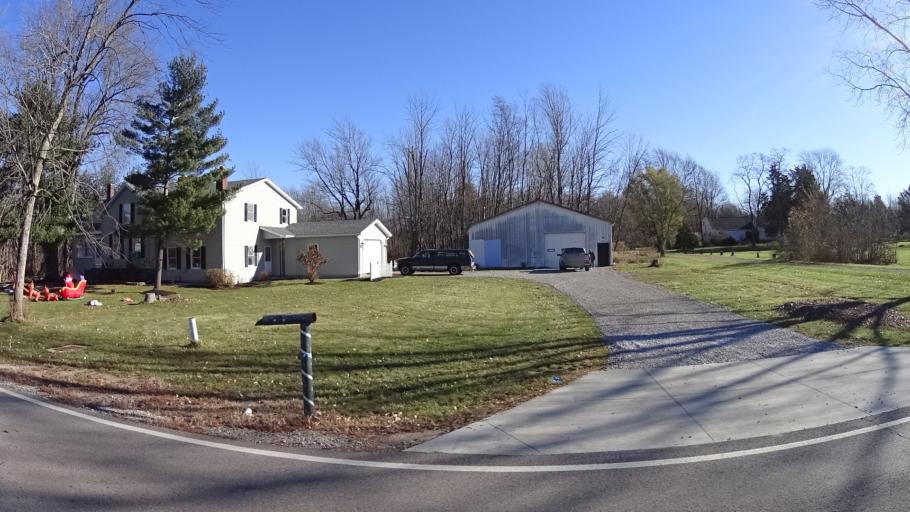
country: US
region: Ohio
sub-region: Lorain County
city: Avon Center
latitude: 41.4822
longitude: -81.9886
